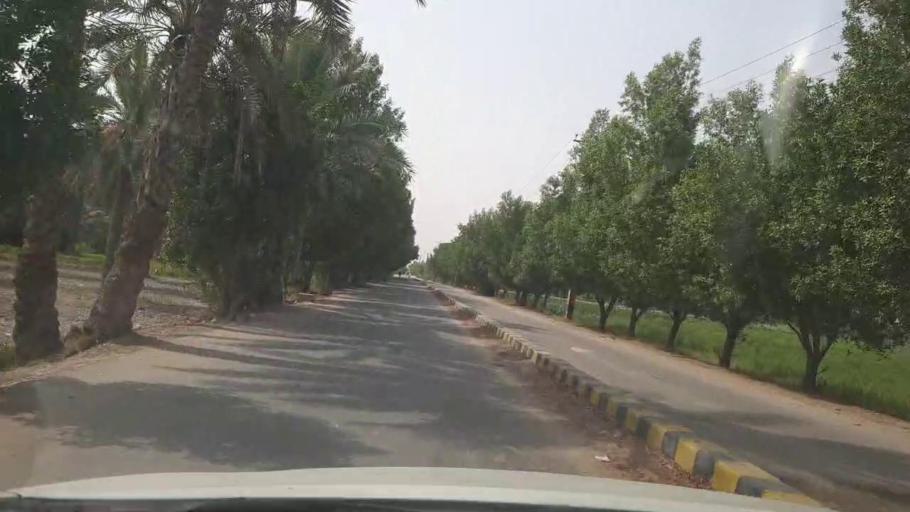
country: PK
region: Sindh
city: Kot Diji
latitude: 27.3521
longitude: 68.7117
